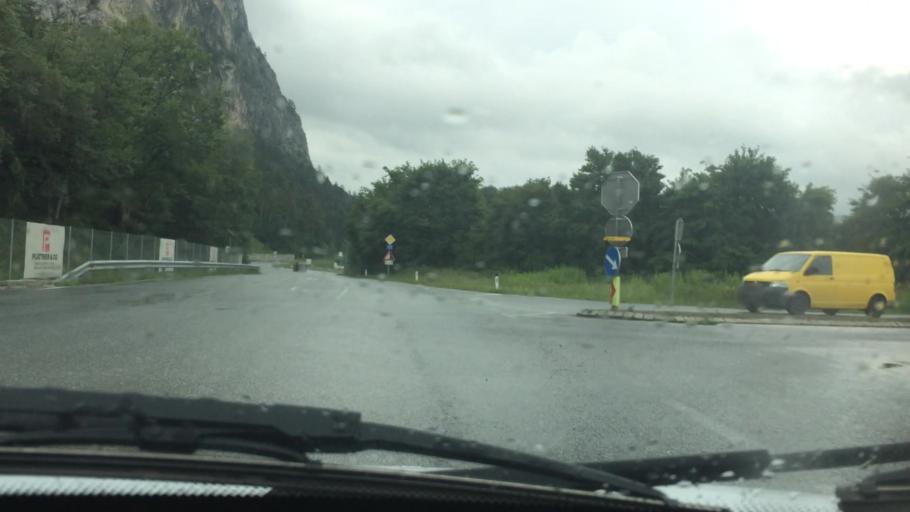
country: AT
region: Tyrol
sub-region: Politischer Bezirk Innsbruck Land
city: Unterperfuss
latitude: 47.2690
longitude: 11.2626
